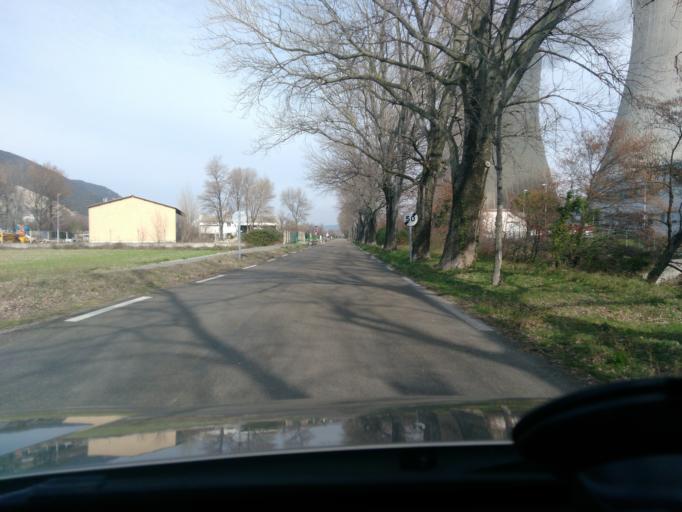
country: FR
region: Rhone-Alpes
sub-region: Departement de l'Ardeche
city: Cruas
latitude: 44.6349
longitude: 4.7502
